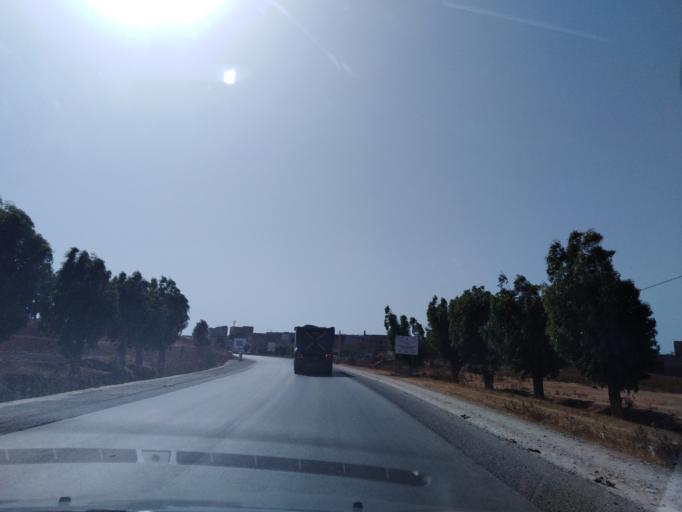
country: MA
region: Doukkala-Abda
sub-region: Safi
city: Safi
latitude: 32.2534
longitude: -8.9767
